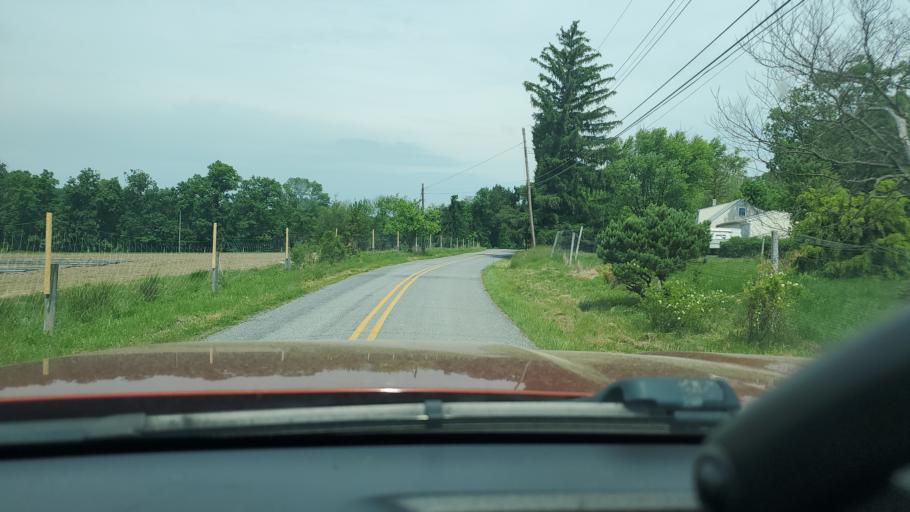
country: US
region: Pennsylvania
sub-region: Montgomery County
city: Woxall
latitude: 40.3157
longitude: -75.5062
